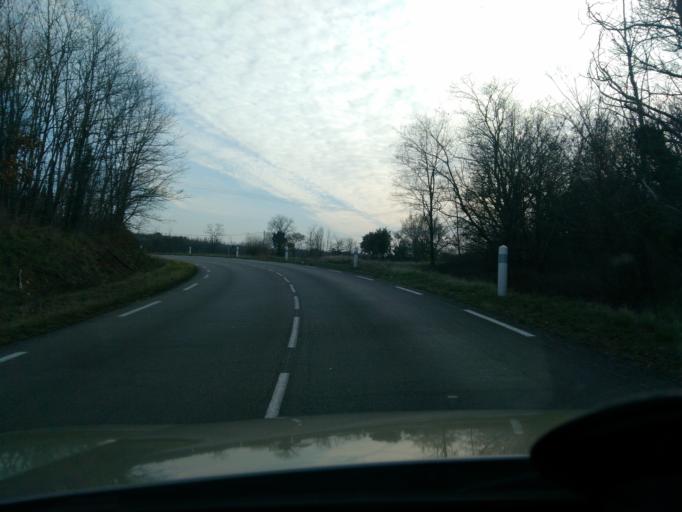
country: FR
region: Rhone-Alpes
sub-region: Departement de la Drome
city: Montelimar
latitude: 44.5275
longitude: 4.7657
